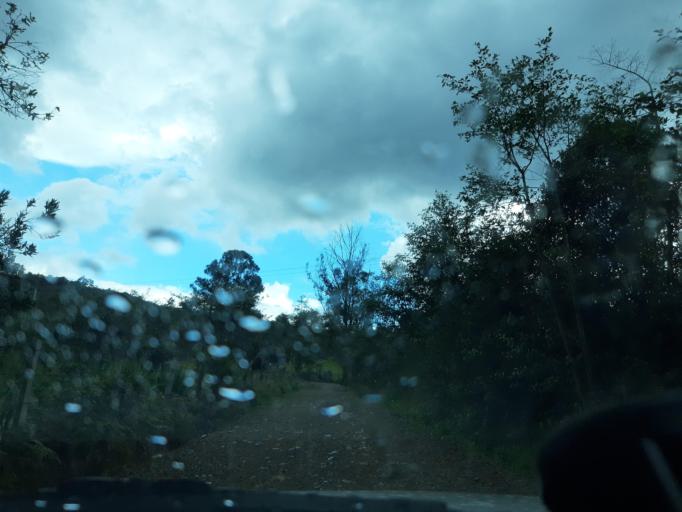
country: CO
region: Boyaca
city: Raquira
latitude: 5.4940
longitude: -73.6954
